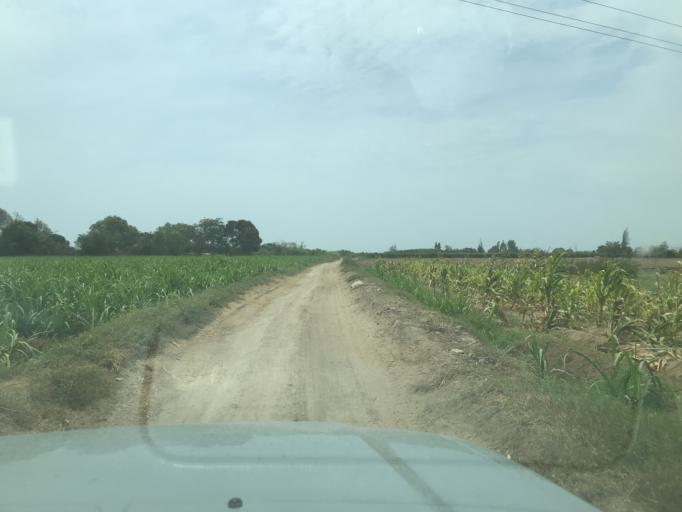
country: PE
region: La Libertad
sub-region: Viru
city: Viru
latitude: -8.4200
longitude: -78.7906
